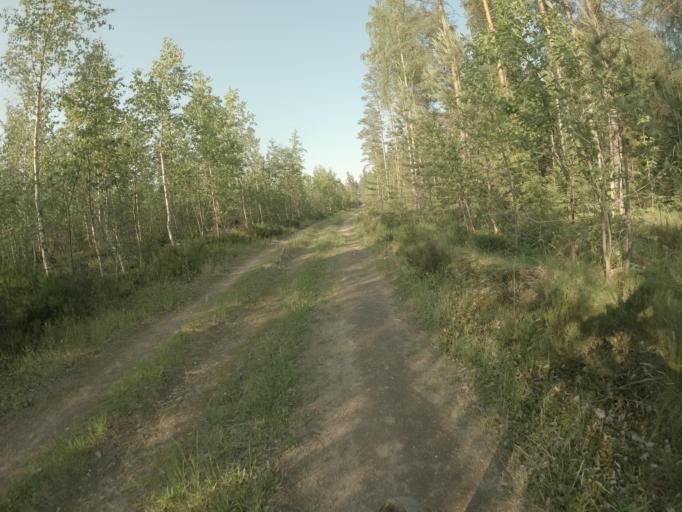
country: RU
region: Leningrad
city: Yakovlevo
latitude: 60.4510
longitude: 29.2538
